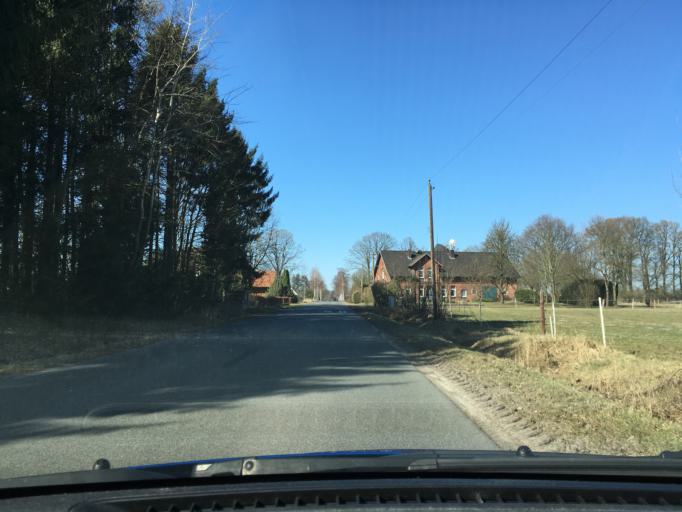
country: DE
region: Lower Saxony
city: Schneverdingen
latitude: 53.0812
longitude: 9.8502
